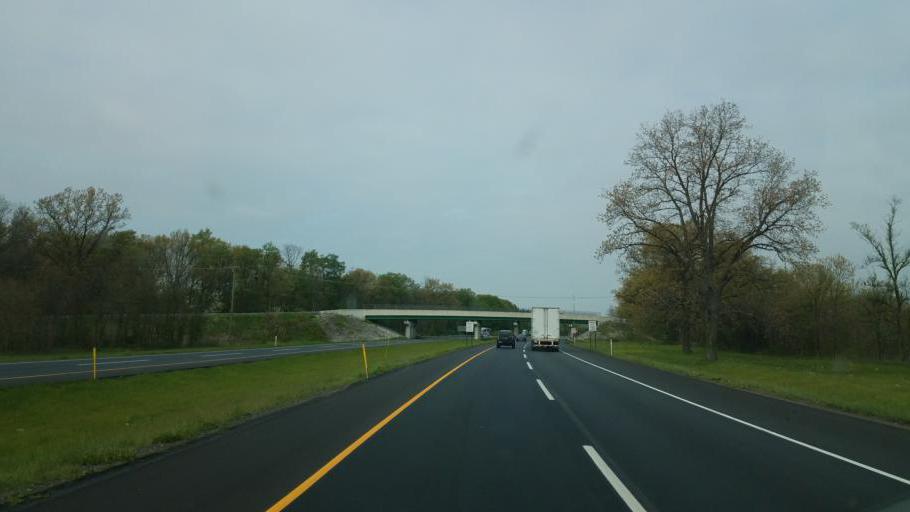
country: US
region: Indiana
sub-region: Saint Joseph County
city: Granger
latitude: 41.7317
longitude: -86.0480
